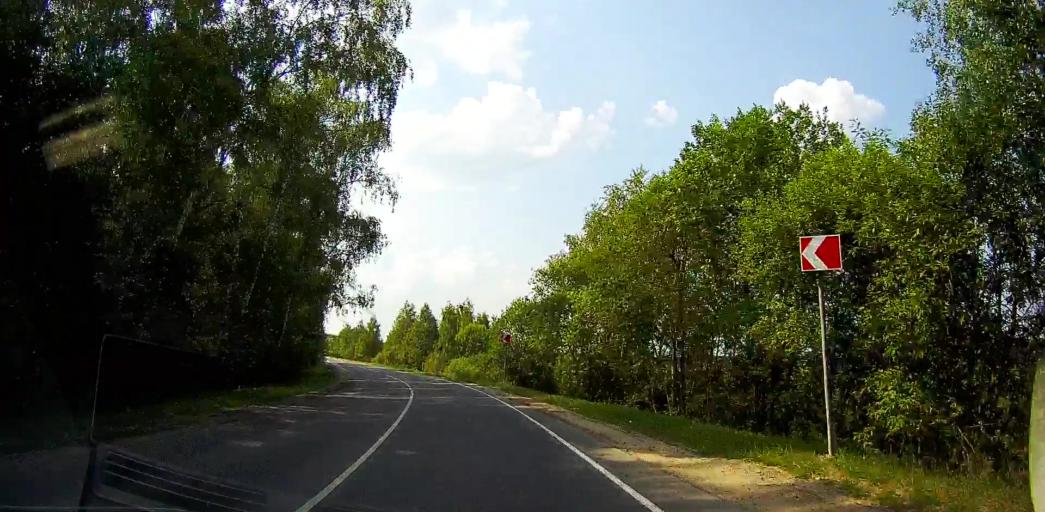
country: RU
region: Moskovskaya
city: Il'inskoye
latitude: 55.1965
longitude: 37.9772
